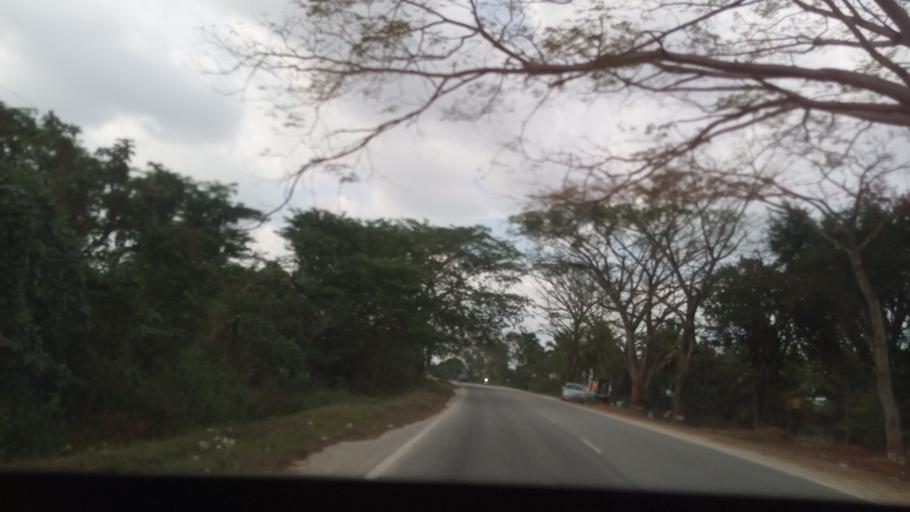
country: IN
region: Karnataka
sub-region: Tumkur
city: Kunigal
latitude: 12.8943
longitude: 77.0443
